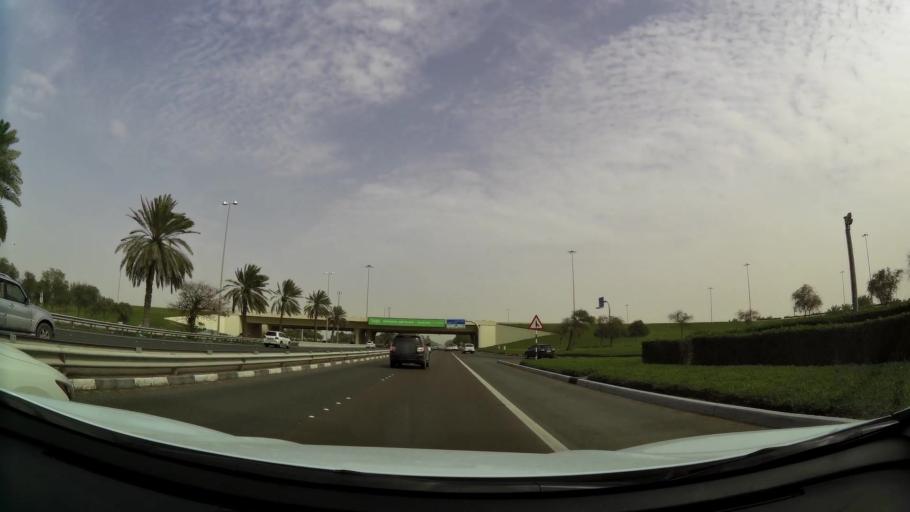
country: AE
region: Abu Dhabi
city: Abu Dhabi
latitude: 24.3971
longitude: 54.5729
